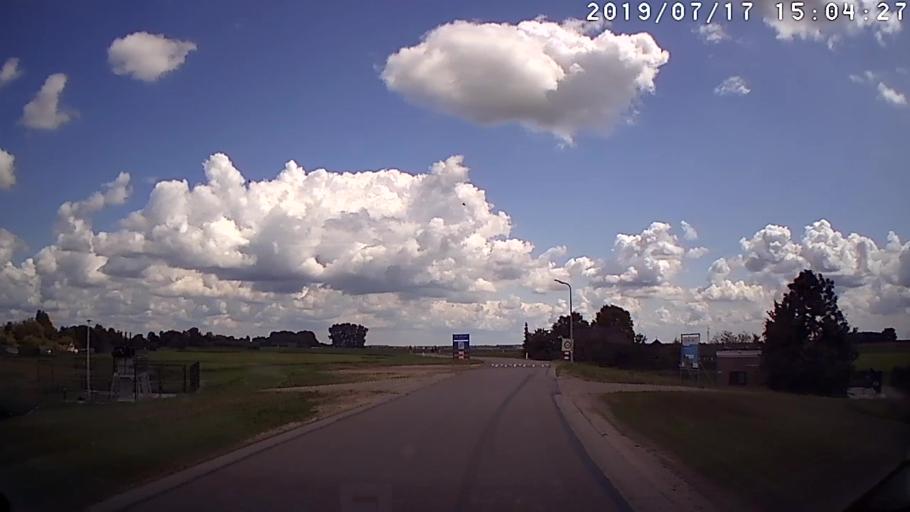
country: NL
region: Overijssel
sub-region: Gemeente Kampen
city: Kampen
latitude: 52.5133
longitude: 5.9622
